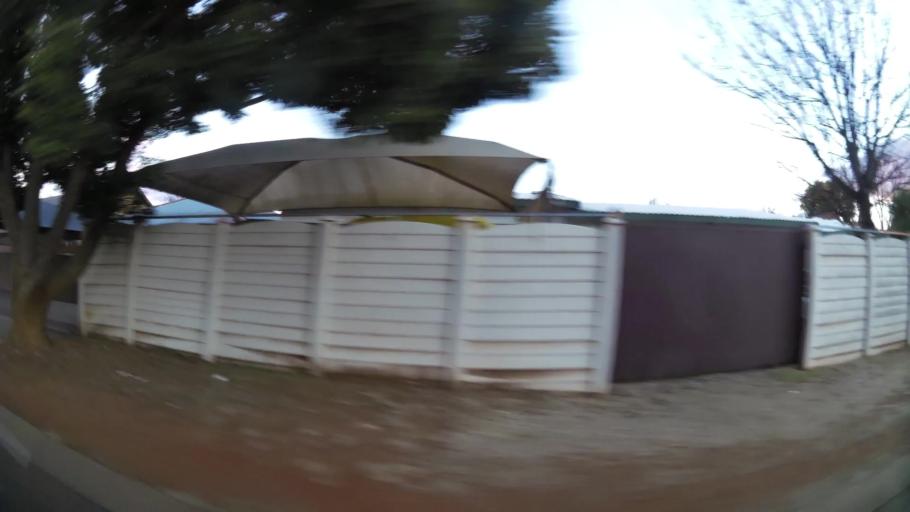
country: ZA
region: North-West
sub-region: Dr Kenneth Kaunda District Municipality
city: Potchefstroom
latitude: -26.7138
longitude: 27.1162
